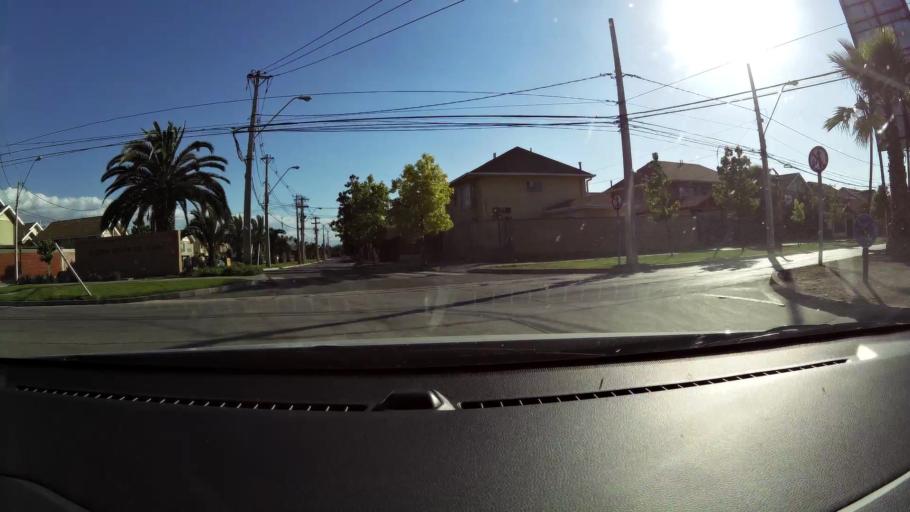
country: CL
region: Santiago Metropolitan
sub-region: Provincia de Maipo
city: San Bernardo
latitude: -33.5508
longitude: -70.7630
